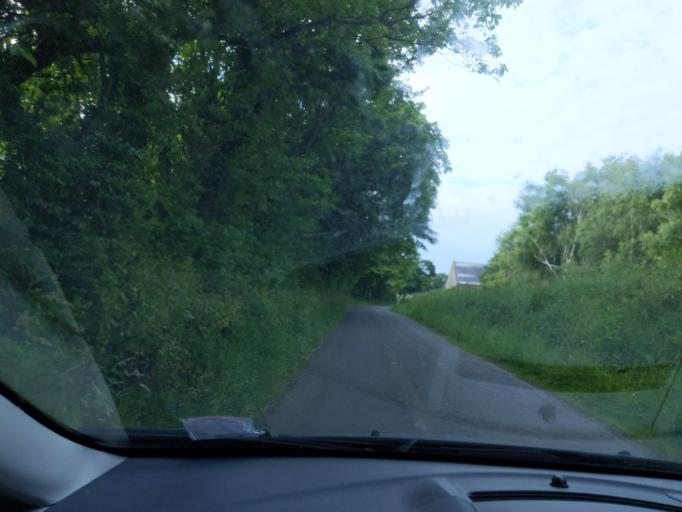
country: IM
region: Ramsey
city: Ramsey
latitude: 54.3624
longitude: -4.4412
